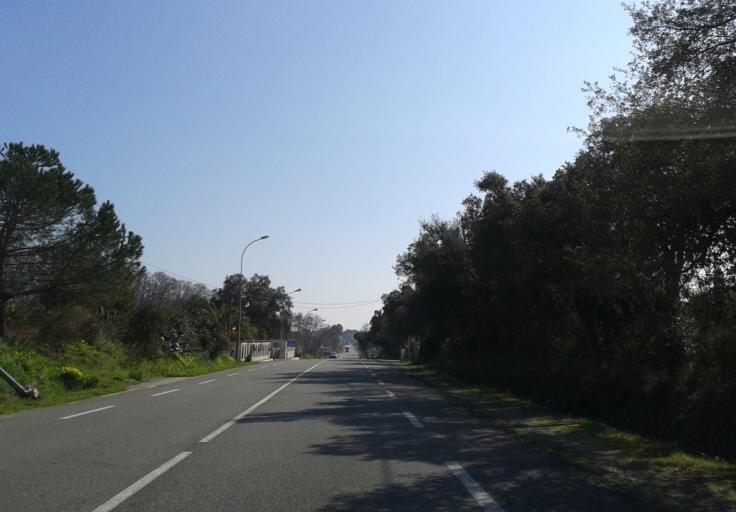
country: FR
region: Corsica
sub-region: Departement de la Haute-Corse
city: Linguizzetta
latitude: 42.2123
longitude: 9.5338
